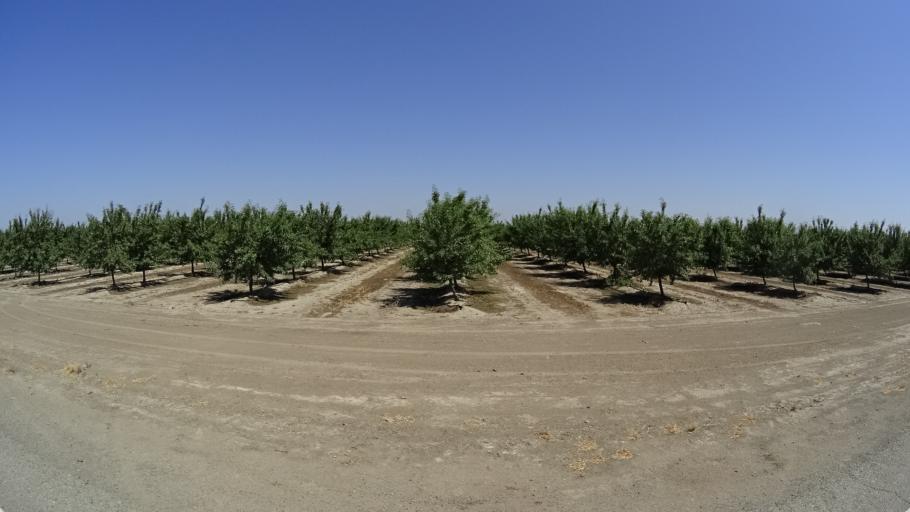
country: US
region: California
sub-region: Kings County
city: Lemoore
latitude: 36.3718
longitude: -119.7711
